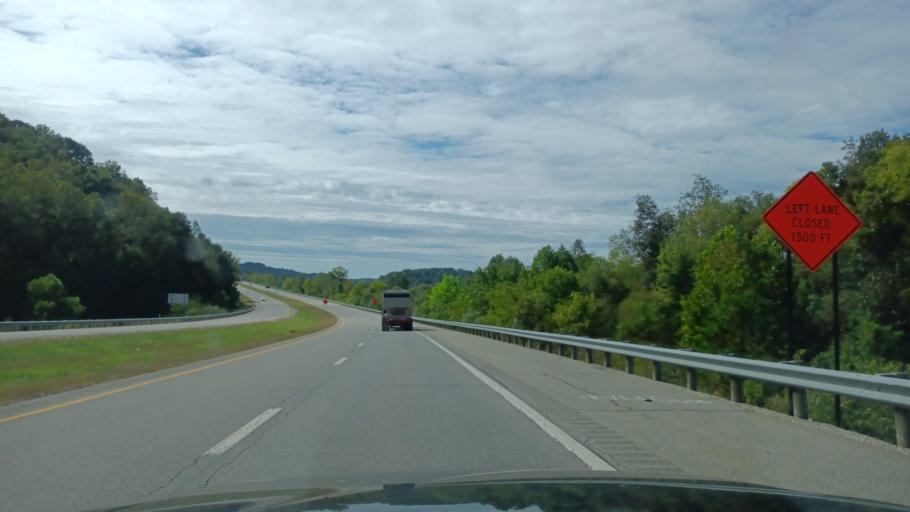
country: US
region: West Virginia
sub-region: Ritchie County
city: Harrisville
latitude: 39.2716
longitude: -81.0402
